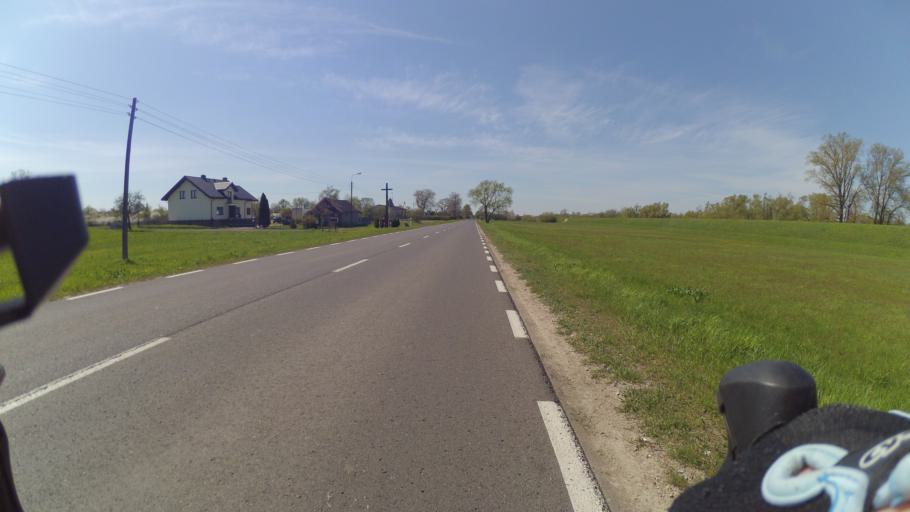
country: PL
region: Masovian Voivodeship
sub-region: Powiat plonski
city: Czerwinsk Nad Wisla
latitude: 52.3774
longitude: 20.3493
